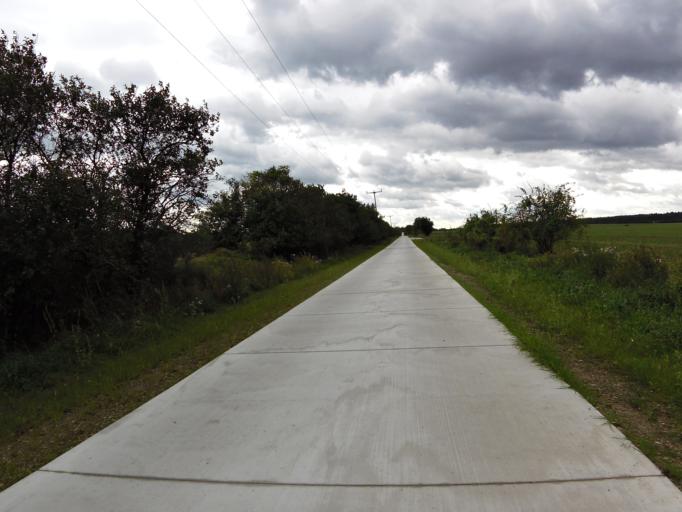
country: DE
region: Saxony-Anhalt
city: Arneburg
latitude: 52.6450
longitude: 12.0037
